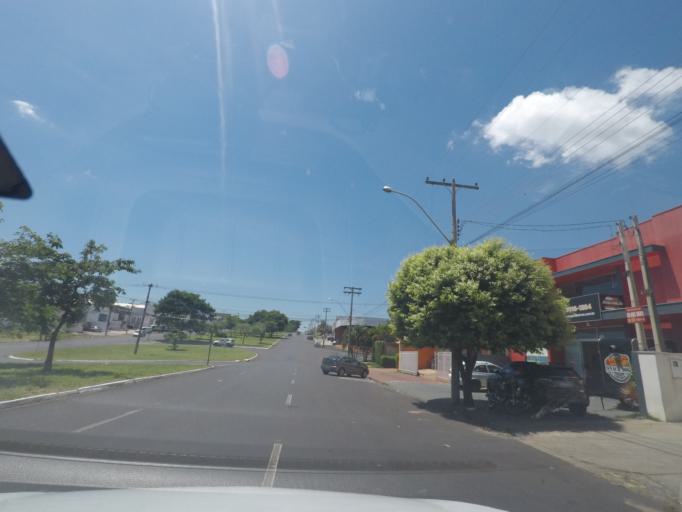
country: BR
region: Sao Paulo
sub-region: Matao
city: Matao
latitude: -21.6184
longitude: -48.3606
